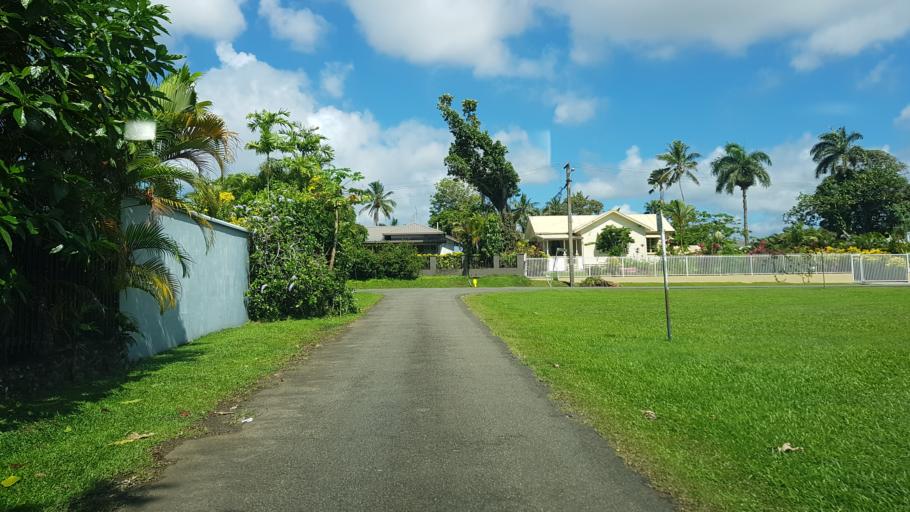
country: FJ
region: Central
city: Suva
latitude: -18.1481
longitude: 178.4546
